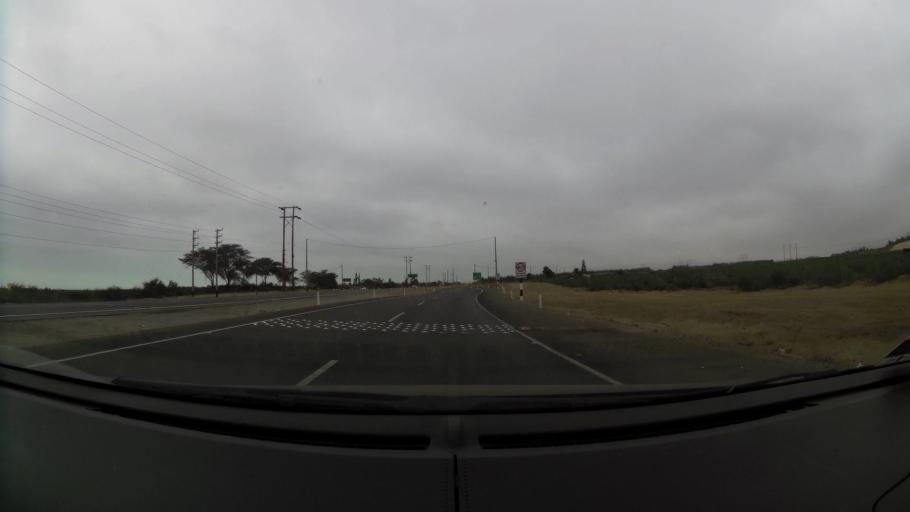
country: PE
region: La Libertad
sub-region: Viru
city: Viru
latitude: -8.3726
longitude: -78.8647
